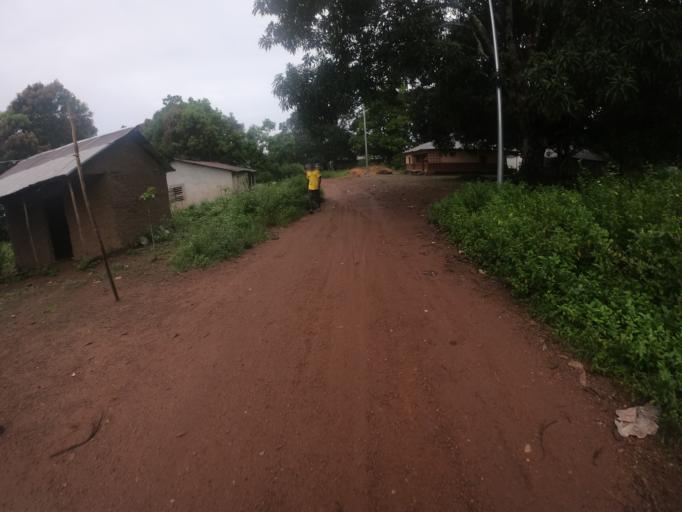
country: SL
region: Northern Province
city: Port Loko
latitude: 8.4924
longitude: -12.7502
